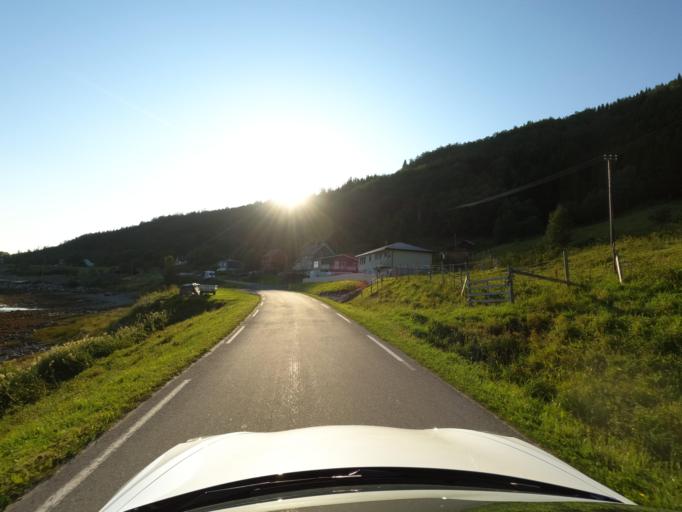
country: NO
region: Nordland
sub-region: Ballangen
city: Ballangen
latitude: 68.4606
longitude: 16.7424
